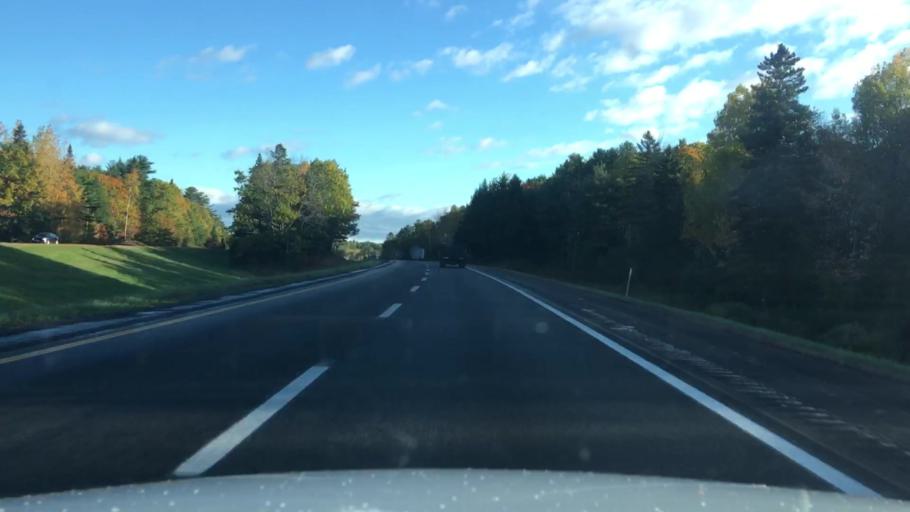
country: US
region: Maine
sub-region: Penobscot County
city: Veazie
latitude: 44.8646
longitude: -68.7096
